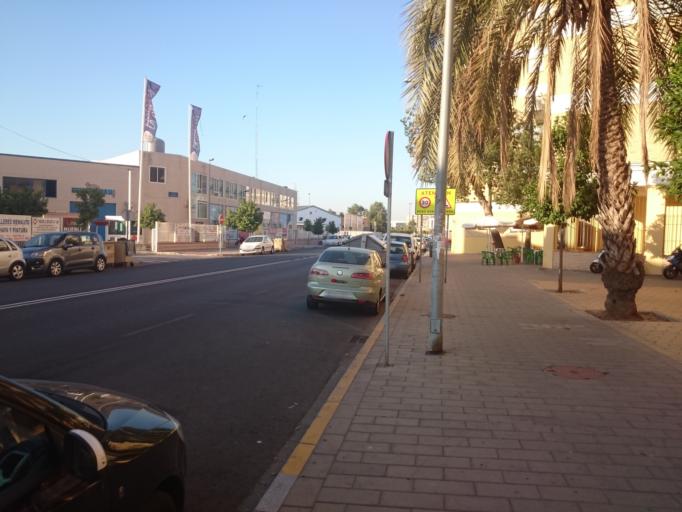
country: ES
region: Andalusia
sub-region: Provincia de Sevilla
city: Sevilla
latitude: 37.3932
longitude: -5.9579
